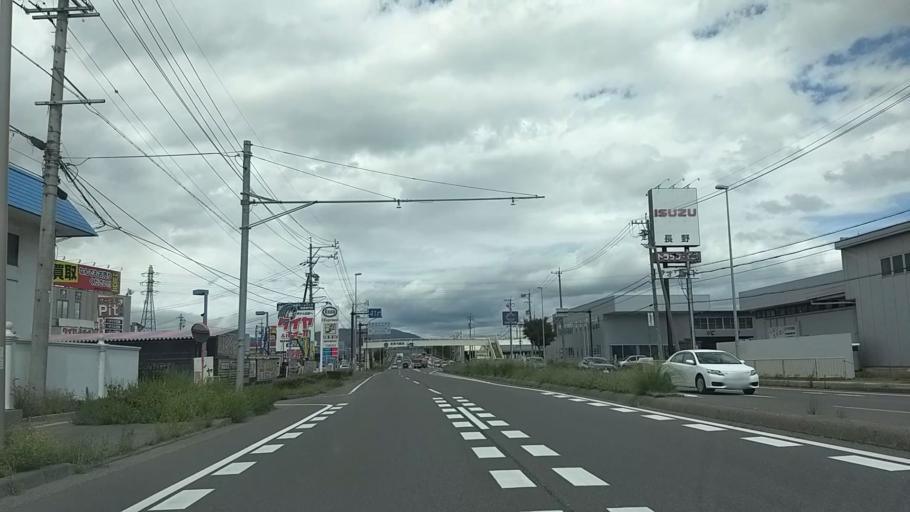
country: JP
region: Nagano
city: Nagano-shi
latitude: 36.6126
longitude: 138.1969
